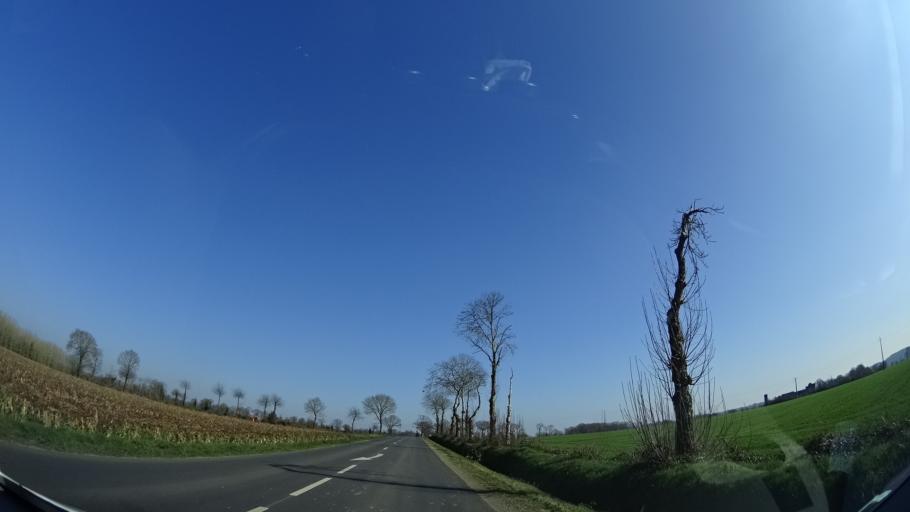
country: FR
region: Brittany
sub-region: Departement d'Ille-et-Vilaine
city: Meillac
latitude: 48.4096
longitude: -1.7941
